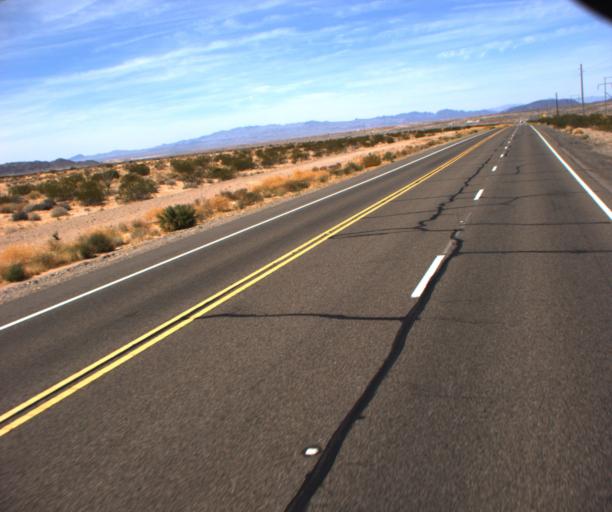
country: US
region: Arizona
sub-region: La Paz County
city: Parker
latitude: 33.9643
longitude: -114.2169
